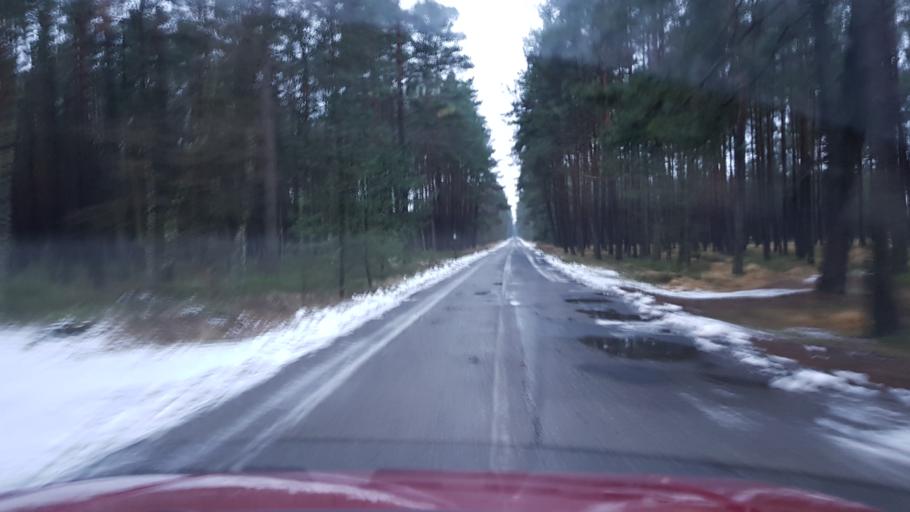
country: PL
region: West Pomeranian Voivodeship
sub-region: Powiat goleniowski
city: Goleniow
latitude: 53.4828
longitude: 14.8486
